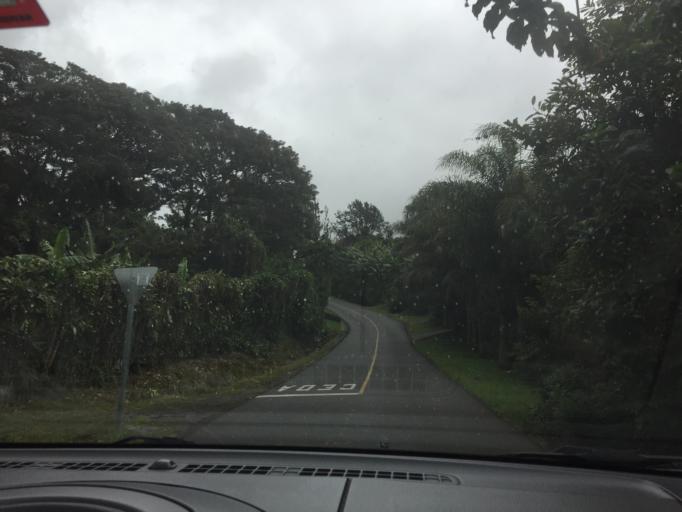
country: CR
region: Heredia
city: Angeles
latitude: 10.0122
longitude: -84.0333
